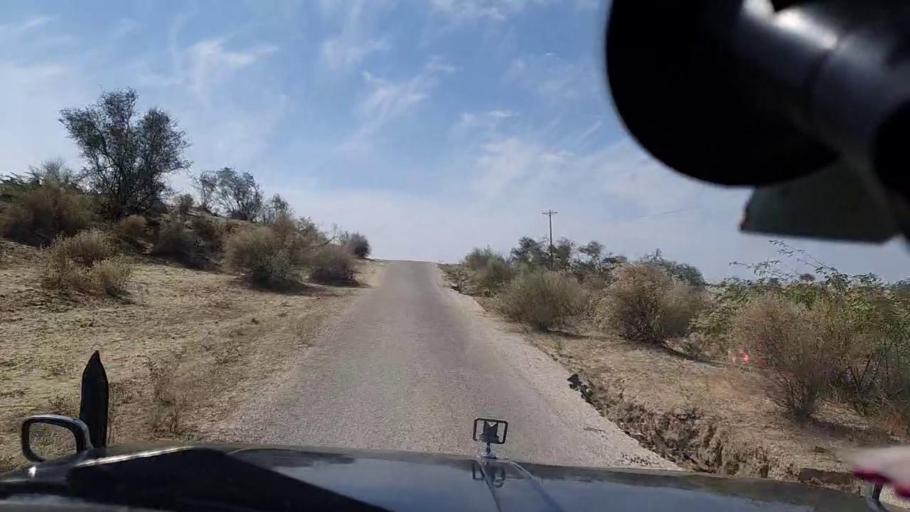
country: PK
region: Sindh
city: Diplo
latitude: 24.3802
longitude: 69.5848
